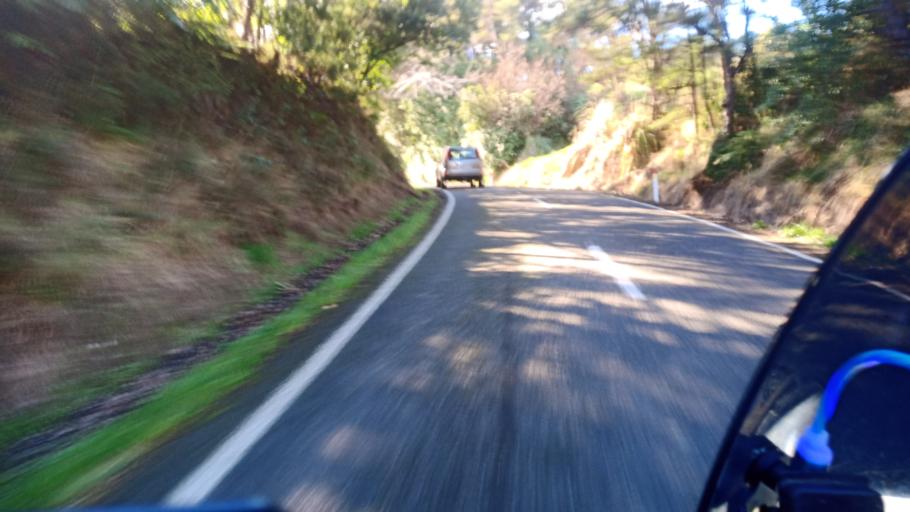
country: NZ
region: Gisborne
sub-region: Gisborne District
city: Gisborne
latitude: -38.2515
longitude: 178.3023
